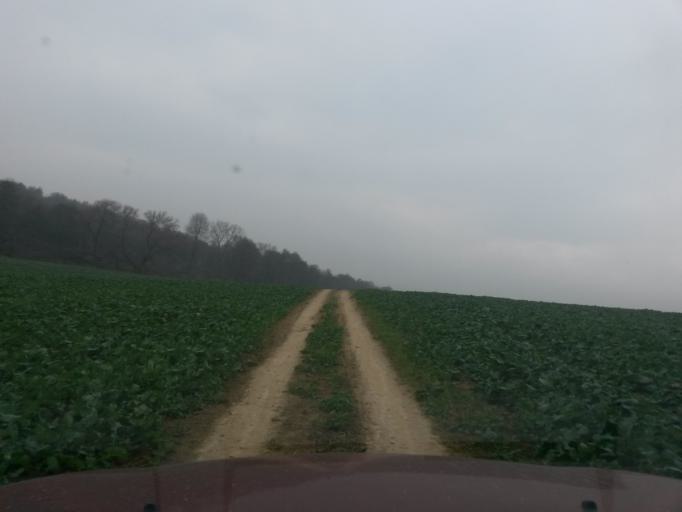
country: SK
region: Presovsky
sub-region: Okres Presov
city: Presov
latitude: 48.8871
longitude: 21.2881
